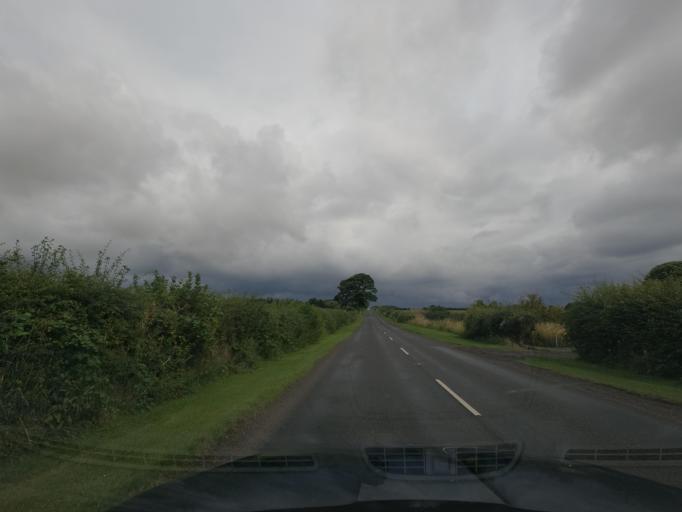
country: GB
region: England
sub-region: Northumberland
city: Ancroft
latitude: 55.7131
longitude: -1.9937
